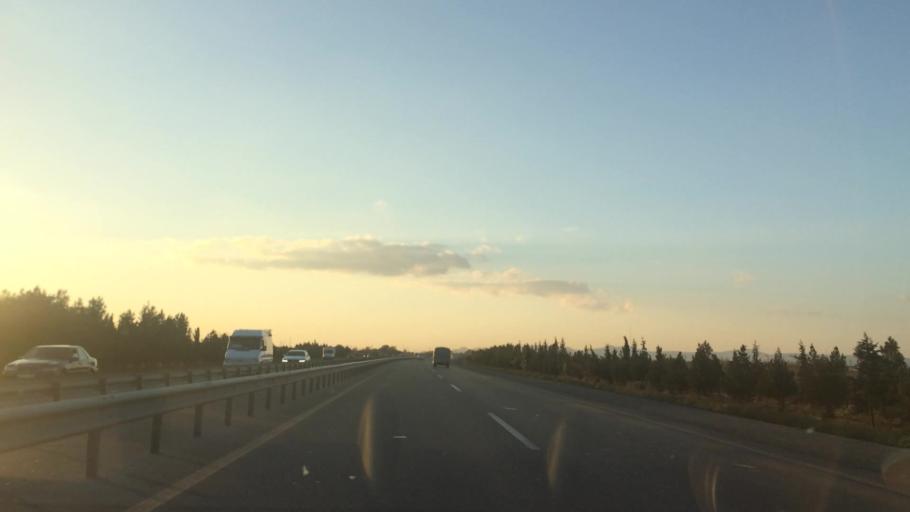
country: AZ
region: Haciqabul
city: Haciqabul
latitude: 40.0236
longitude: 49.1165
